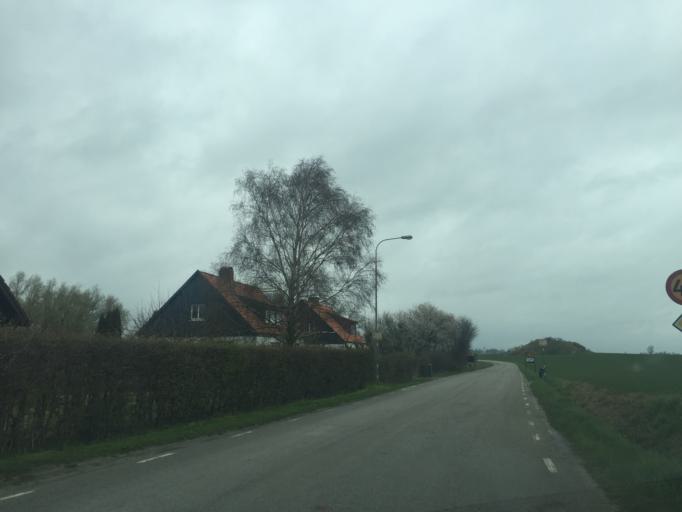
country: SE
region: Skane
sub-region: Skurups Kommun
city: Skivarp
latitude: 55.4261
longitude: 13.5850
